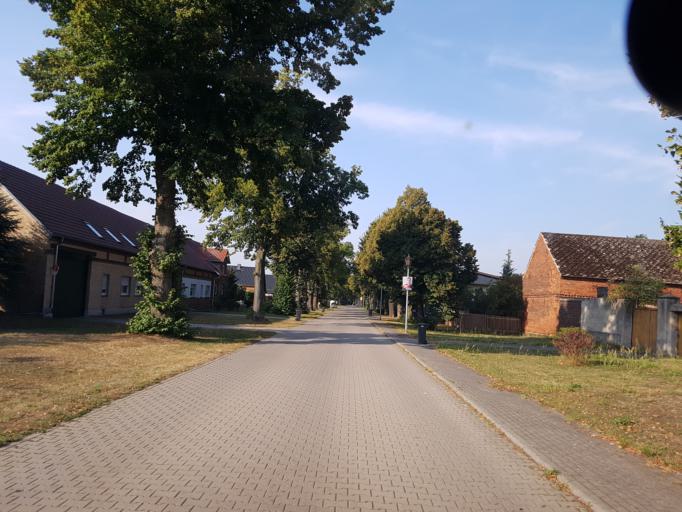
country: DE
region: Brandenburg
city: Finsterwalde
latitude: 51.6913
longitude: 13.7199
